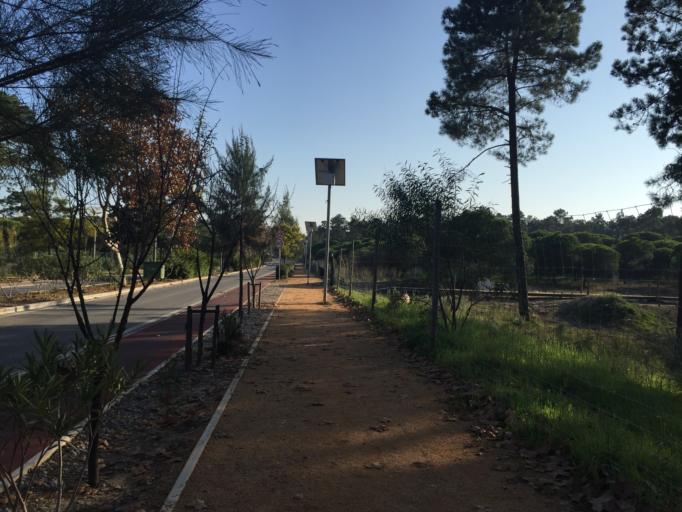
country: PT
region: Faro
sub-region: Vila Real de Santo Antonio
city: Vila Real de Santo Antonio
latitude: 37.1898
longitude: -7.4236
